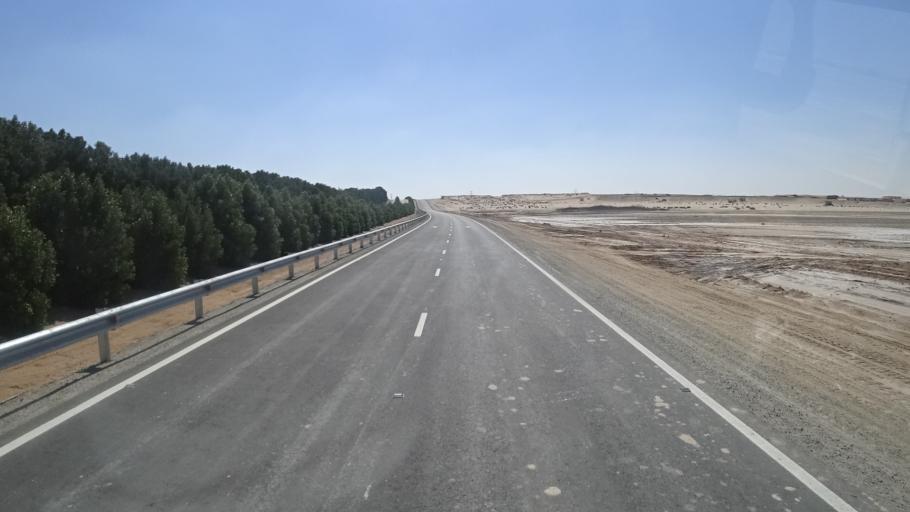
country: AE
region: Abu Dhabi
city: Abu Dhabi
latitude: 24.1886
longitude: 54.6978
